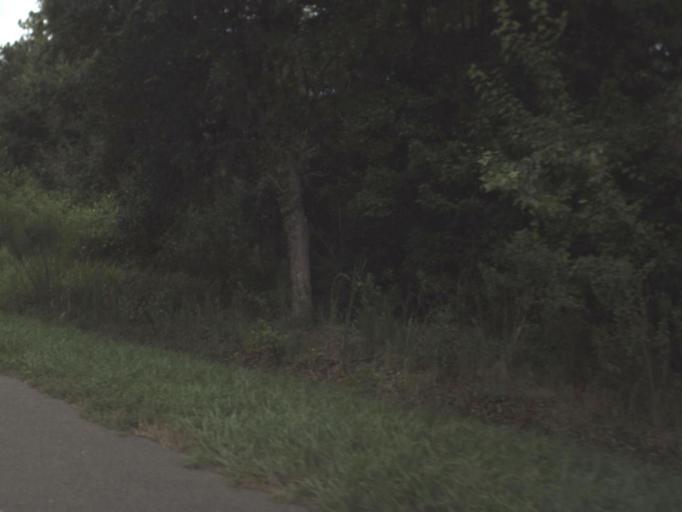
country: US
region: Florida
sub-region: Polk County
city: Frostproof
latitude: 27.7335
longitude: -81.6178
